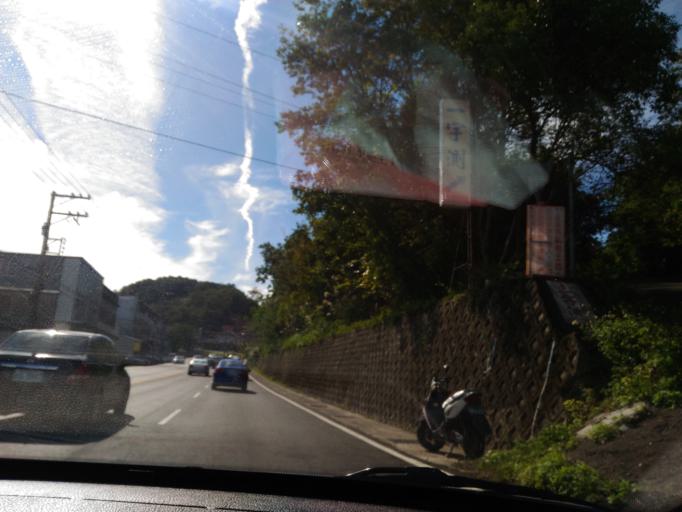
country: TW
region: Taiwan
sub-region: Hsinchu
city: Zhubei
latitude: 24.7236
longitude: 121.0775
